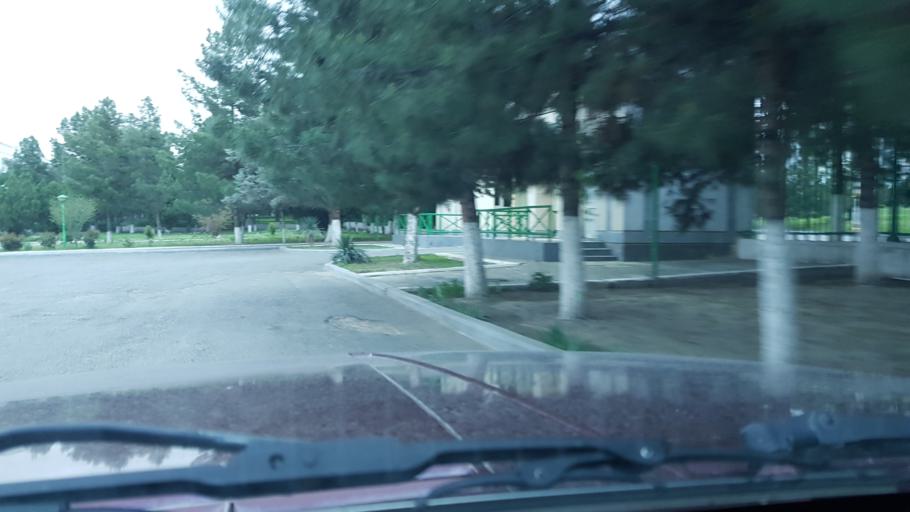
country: TM
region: Ahal
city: Ashgabat
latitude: 37.8840
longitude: 58.3617
